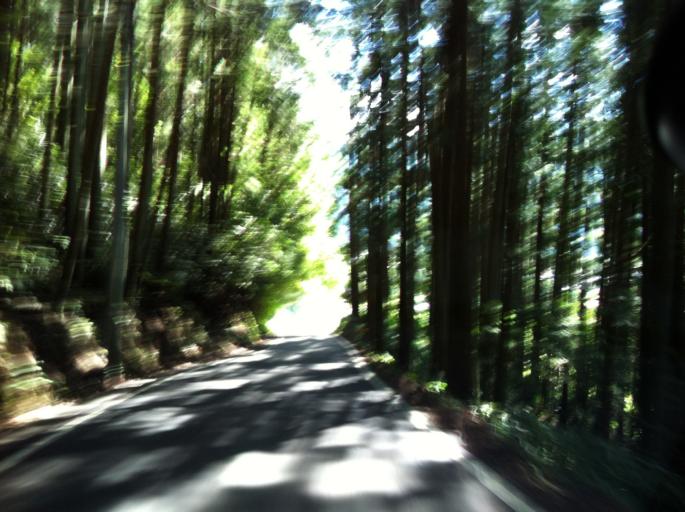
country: JP
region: Shizuoka
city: Kanaya
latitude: 35.0806
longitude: 138.1128
